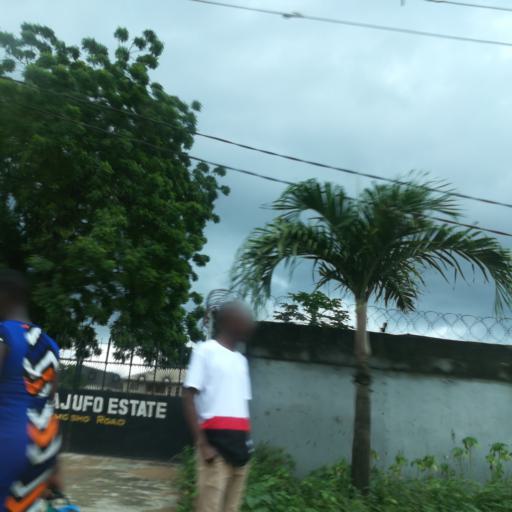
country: NG
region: Lagos
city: Agege
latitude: 6.6105
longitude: 3.3029
